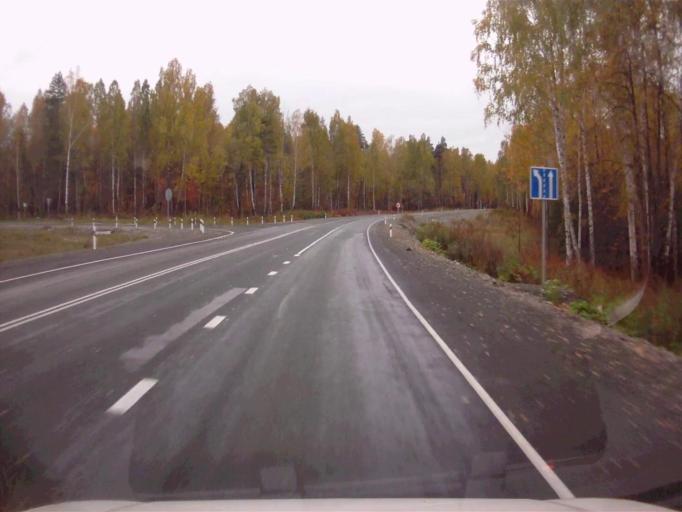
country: RU
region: Chelyabinsk
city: Nyazepetrovsk
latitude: 56.0589
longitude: 59.7324
